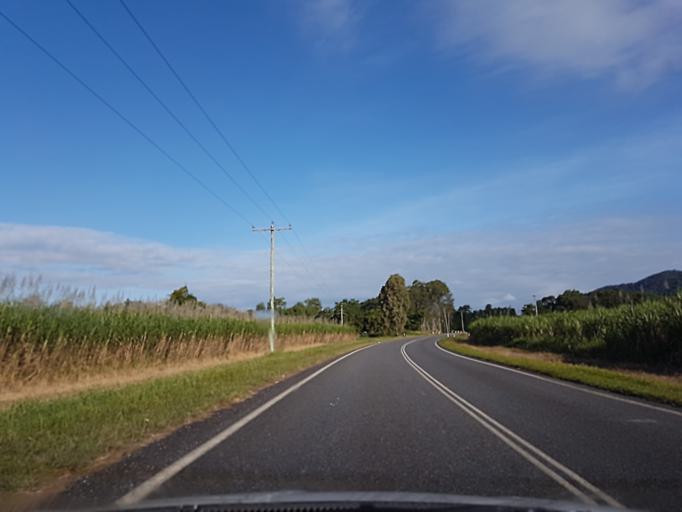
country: AU
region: Queensland
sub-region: Cairns
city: Port Douglas
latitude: -16.3350
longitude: 145.4102
